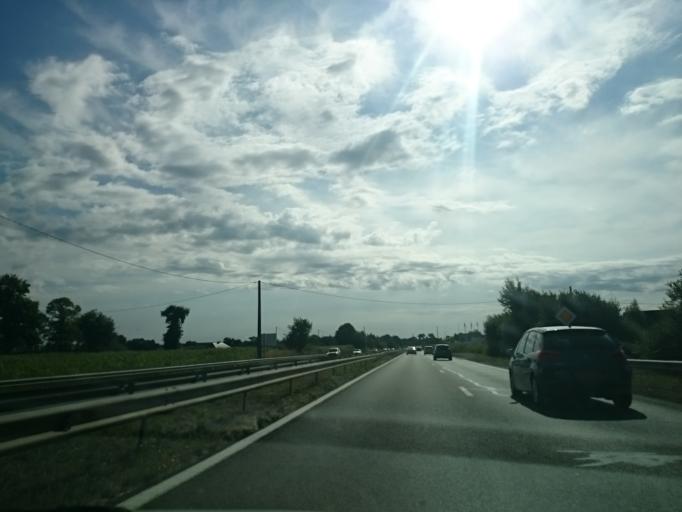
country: FR
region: Brittany
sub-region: Departement d'Ille-et-Vilaine
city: Saint-Gilles
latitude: 48.1588
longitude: -1.8253
